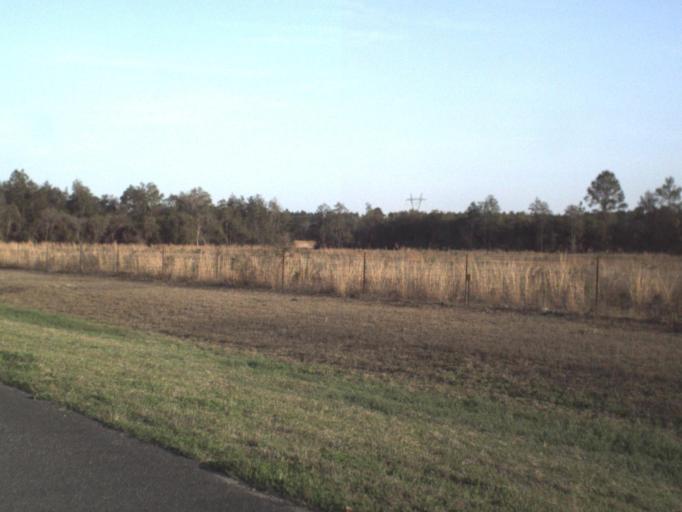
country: US
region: Florida
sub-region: Bay County
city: Lynn Haven
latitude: 30.4397
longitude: -85.7764
